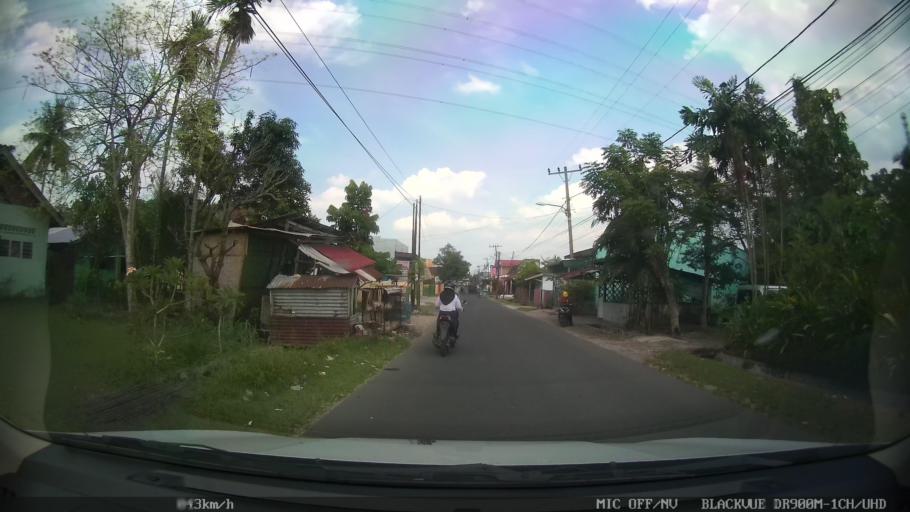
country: ID
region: North Sumatra
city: Binjai
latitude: 3.6131
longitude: 98.5057
